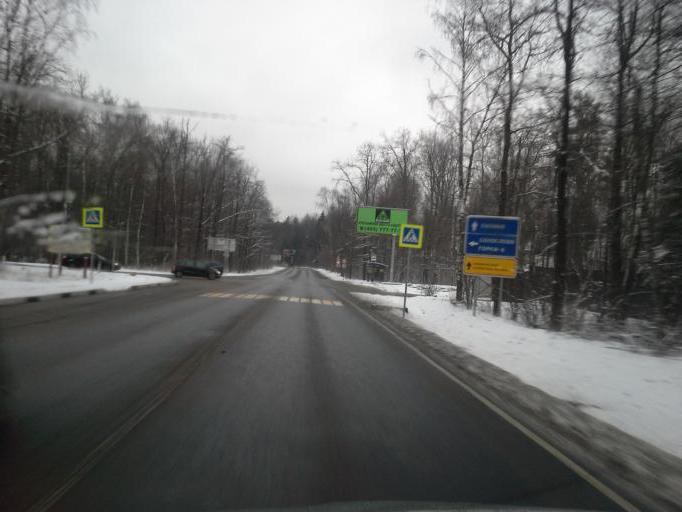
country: RU
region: Moskovskaya
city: Gorki Vtoryye
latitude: 55.6911
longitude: 37.1333
